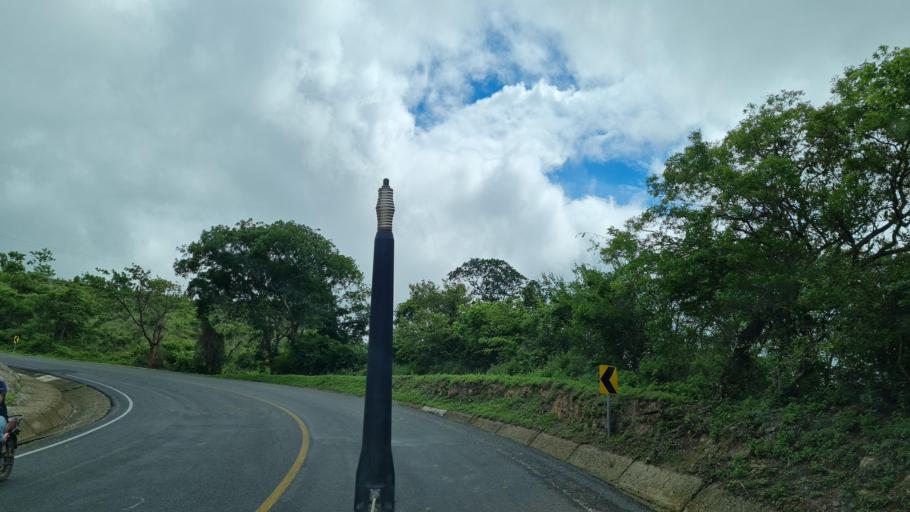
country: NI
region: Matagalpa
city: Terrabona
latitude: 12.5837
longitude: -85.9806
